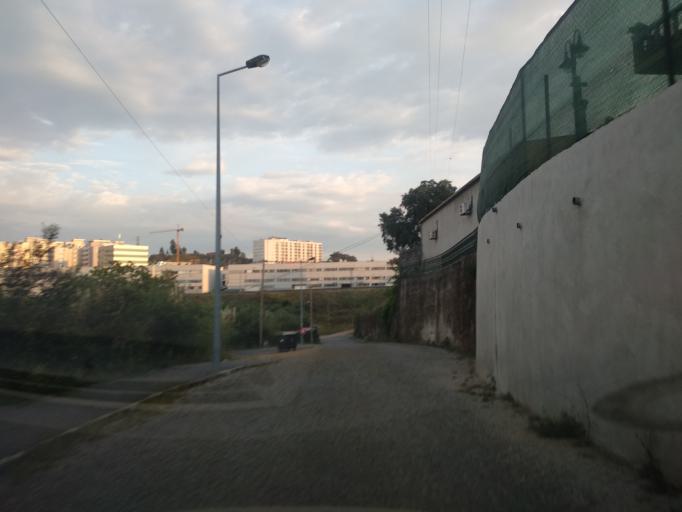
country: PT
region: Braga
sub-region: Braga
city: Braga
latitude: 41.5298
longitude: -8.4511
